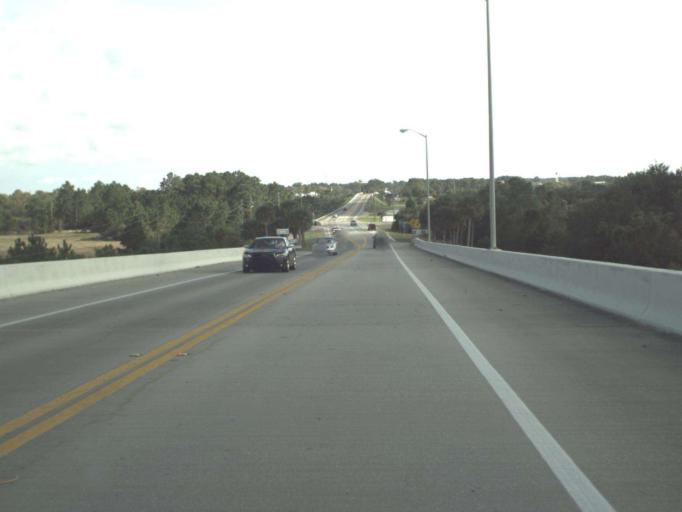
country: US
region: Florida
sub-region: Gulf County
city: Port Saint Joe
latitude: 29.8295
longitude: -85.3119
